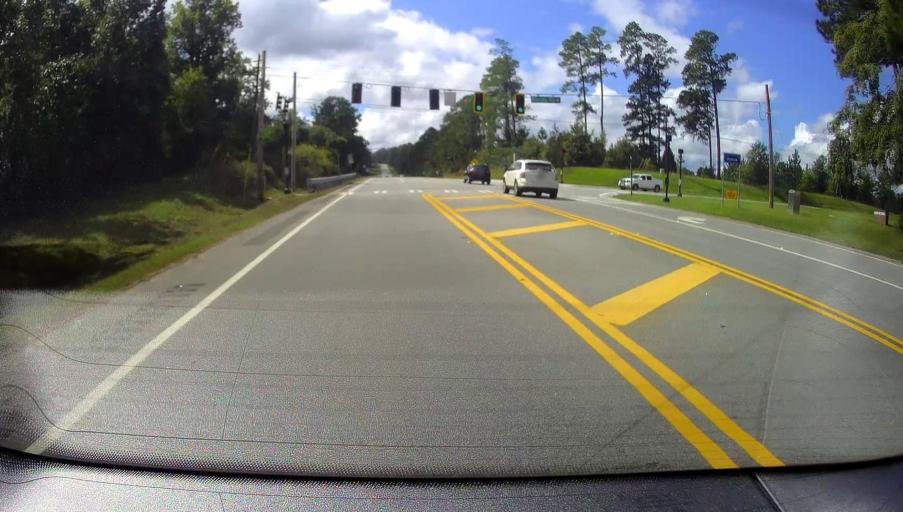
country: US
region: Georgia
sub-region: Baldwin County
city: Milledgeville
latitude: 33.0704
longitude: -83.2600
